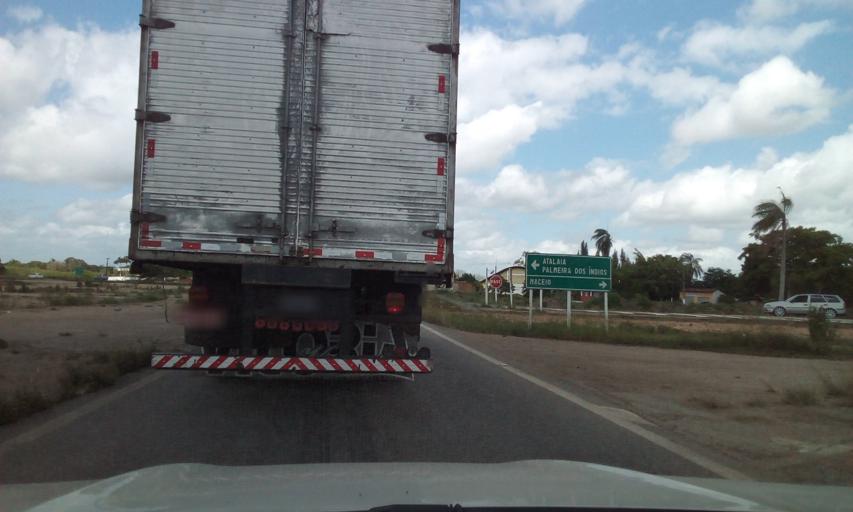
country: BR
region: Alagoas
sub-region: Pilar
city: Pilar
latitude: -9.5670
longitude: -35.9695
